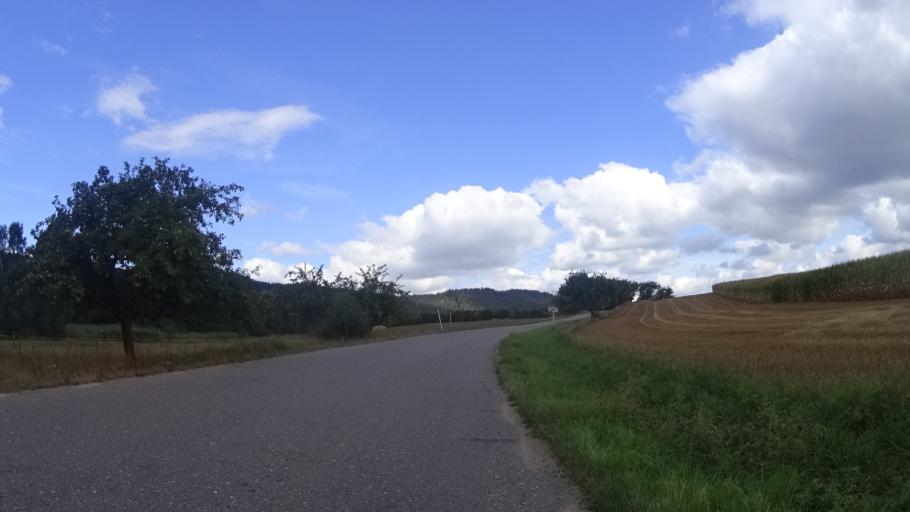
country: CZ
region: Pardubicky
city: Dolni Dobrouc
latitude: 49.9457
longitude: 16.5173
